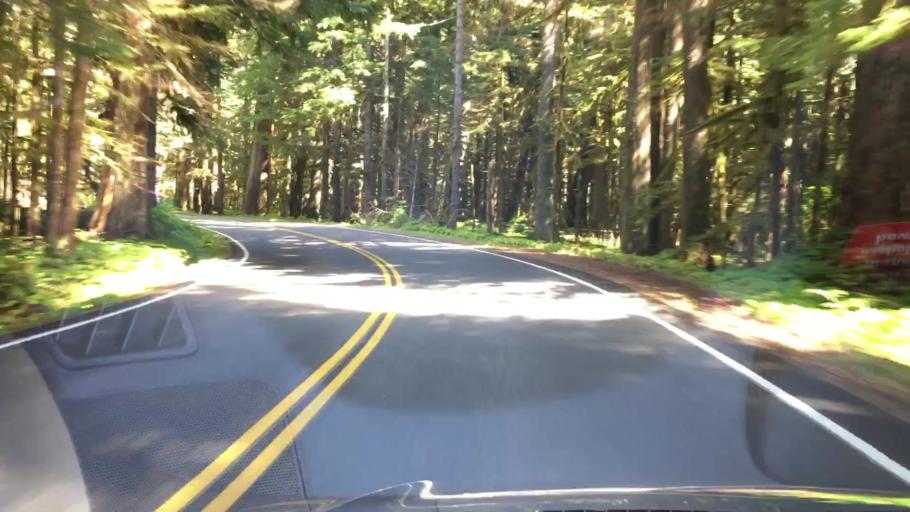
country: US
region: Washington
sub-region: Pierce County
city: Eatonville
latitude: 46.7411
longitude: -121.8903
